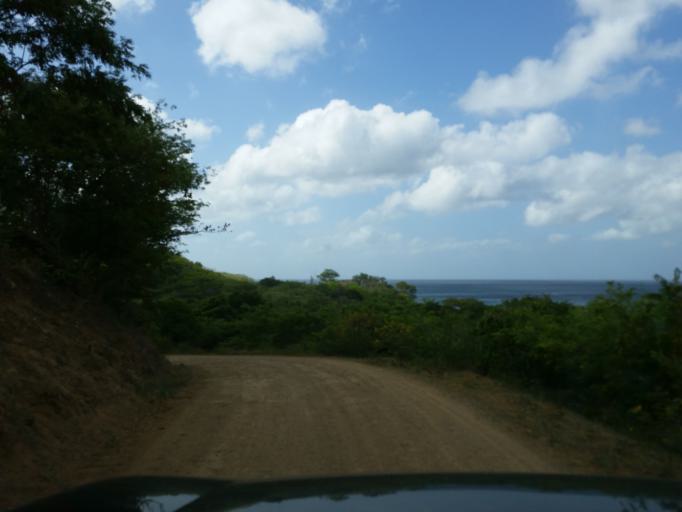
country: NI
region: Rivas
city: San Juan del Sur
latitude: 11.2141
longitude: -85.8407
